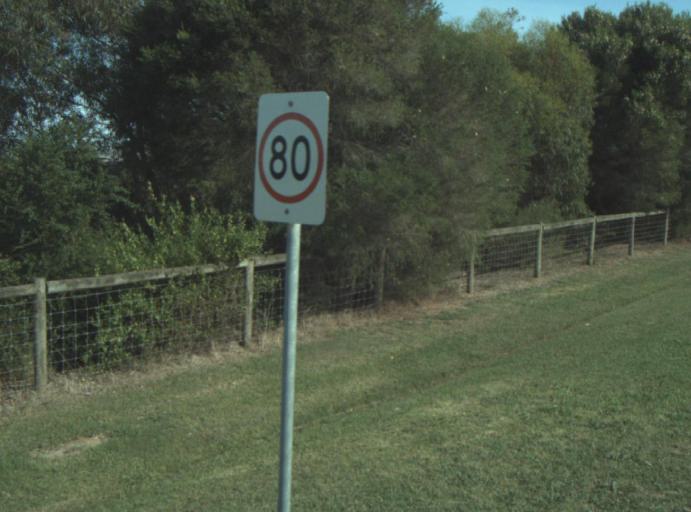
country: AU
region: Victoria
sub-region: Greater Geelong
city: Leopold
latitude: -38.1802
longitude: 144.4381
